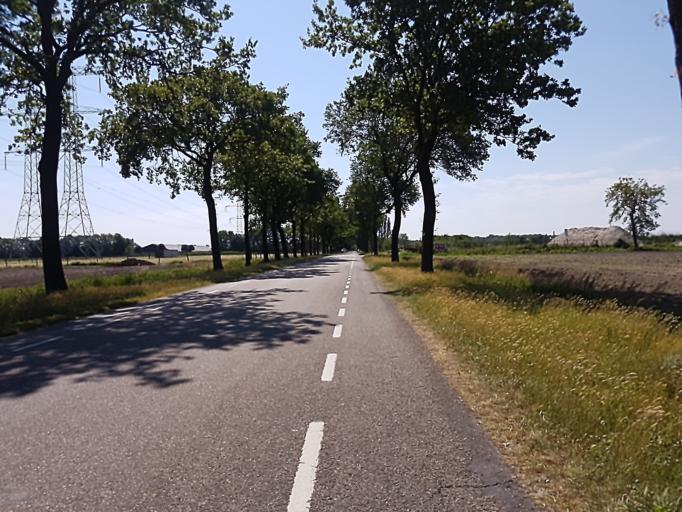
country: NL
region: North Brabant
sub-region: Gemeente Dongen
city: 's Gravenmoer
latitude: 51.6426
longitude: 4.9917
